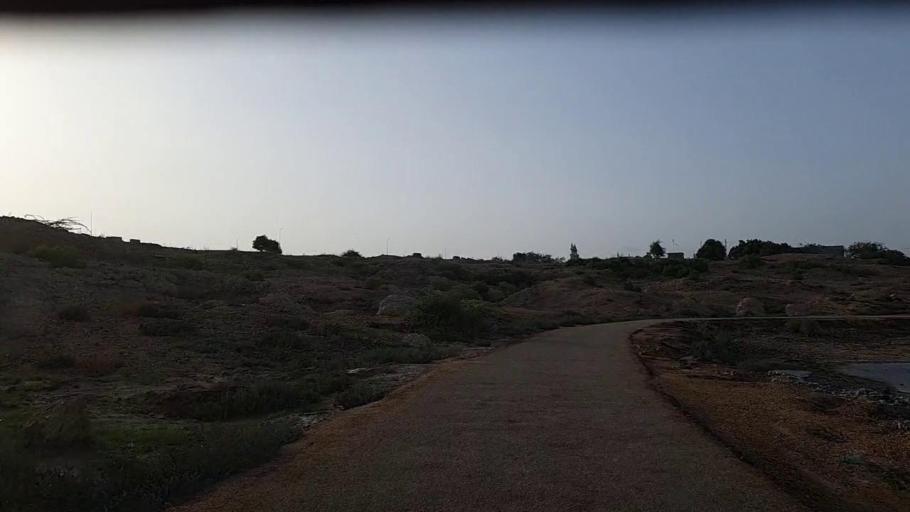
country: PK
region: Sindh
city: Thatta
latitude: 24.7580
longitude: 67.9040
